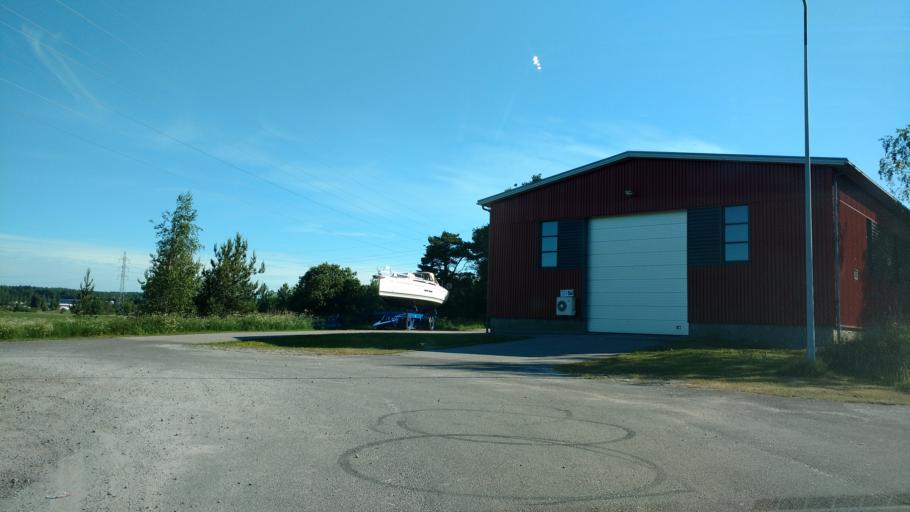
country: FI
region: Varsinais-Suomi
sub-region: Salo
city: Halikko
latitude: 60.3766
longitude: 23.1030
